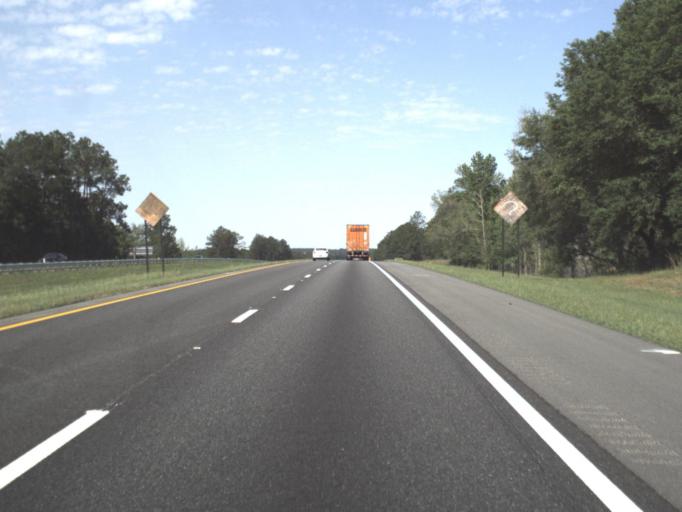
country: US
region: Florida
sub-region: Walton County
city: DeFuniak Springs
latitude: 30.7219
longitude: -85.9166
